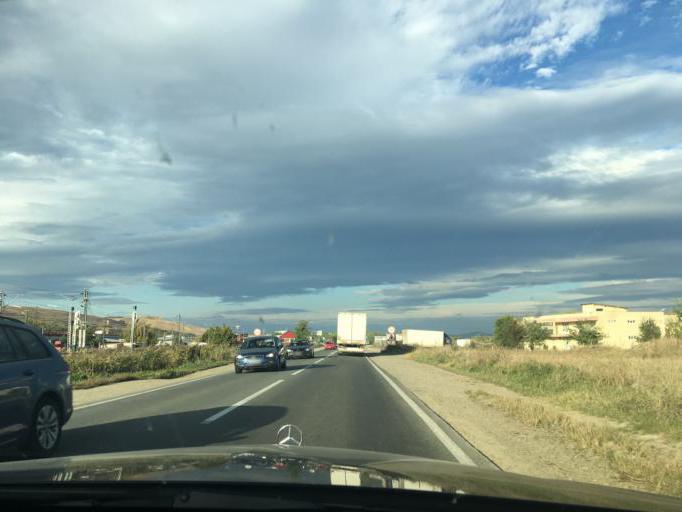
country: RO
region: Alba
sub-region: Municipiul Alba Iulia
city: Barabant
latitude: 46.0993
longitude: 23.6061
